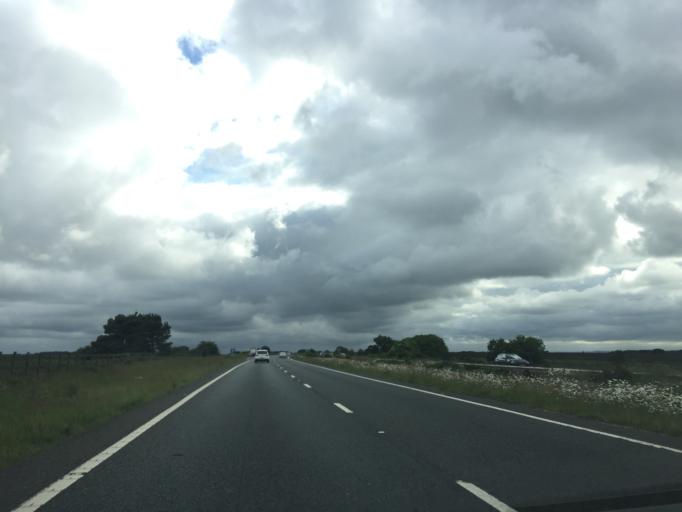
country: GB
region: England
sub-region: Hampshire
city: Ringwood
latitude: 50.8708
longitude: -1.6974
